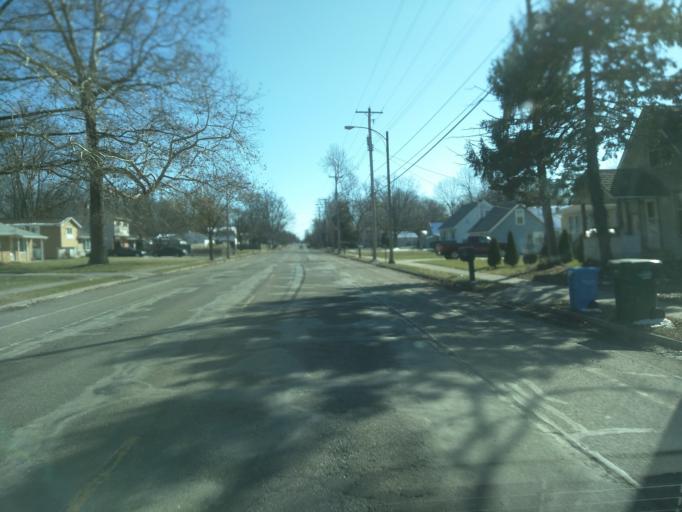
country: US
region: Michigan
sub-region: Ingham County
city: Lansing
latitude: 42.7034
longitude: -84.5822
